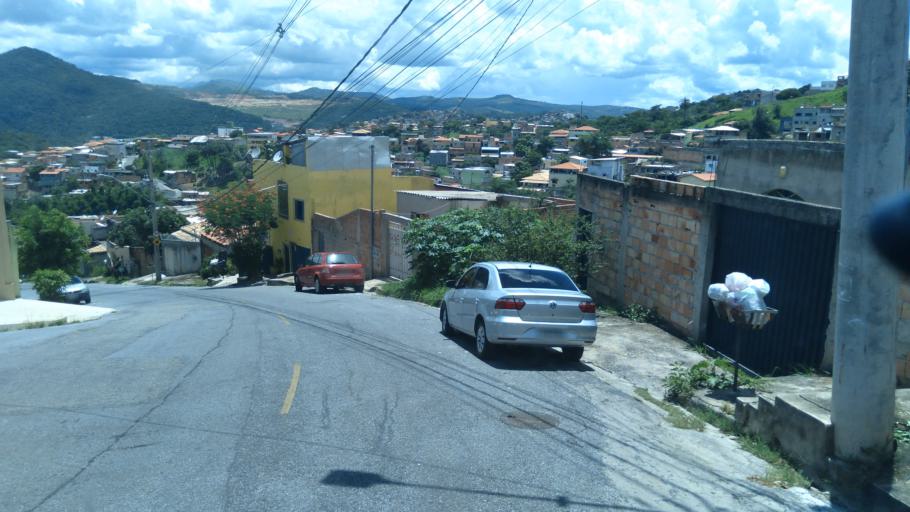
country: BR
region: Minas Gerais
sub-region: Belo Horizonte
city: Belo Horizonte
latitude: -19.8585
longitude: -43.8792
